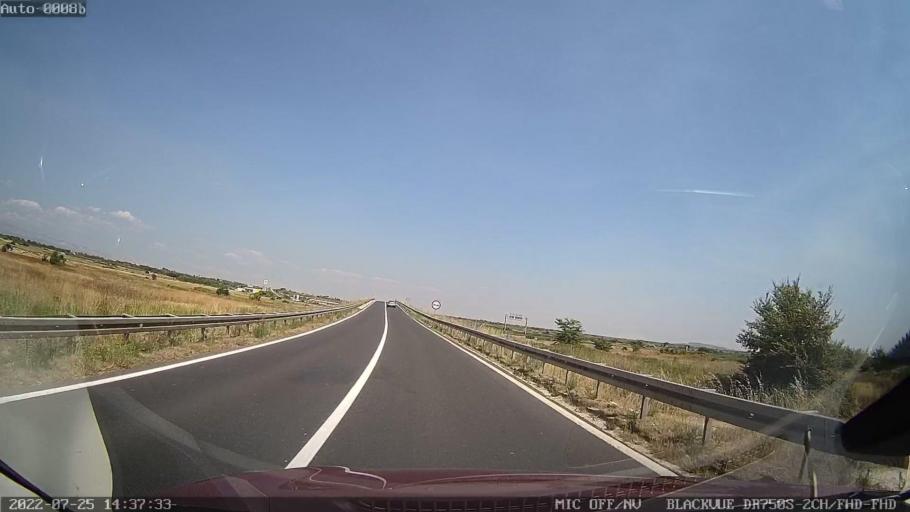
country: HR
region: Zadarska
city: Galovac
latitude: 44.1129
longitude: 15.3991
